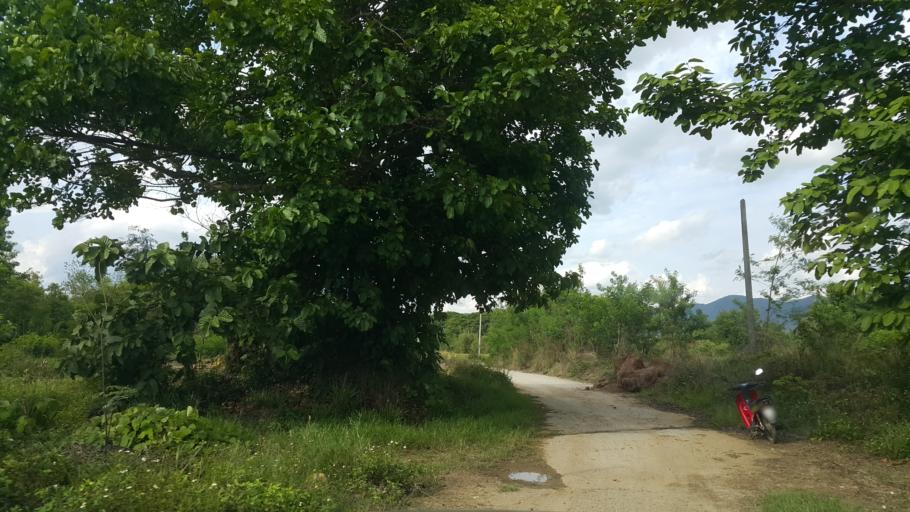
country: TH
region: Chiang Mai
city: Mae On
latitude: 18.7435
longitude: 99.2304
